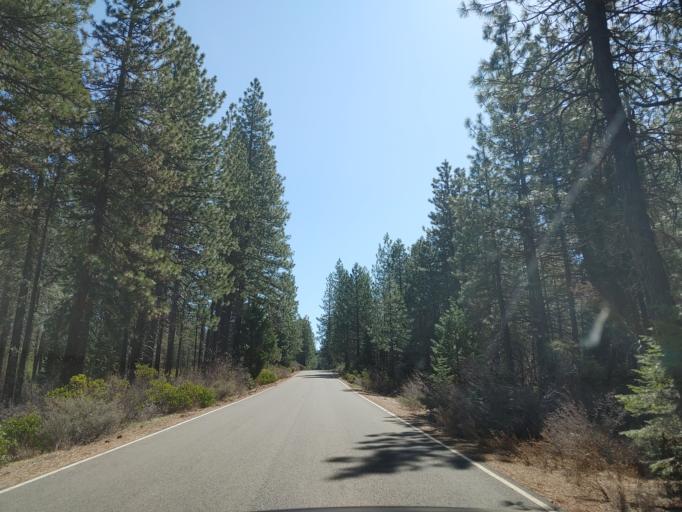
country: US
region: California
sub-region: Siskiyou County
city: McCloud
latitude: 41.2470
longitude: -122.0211
